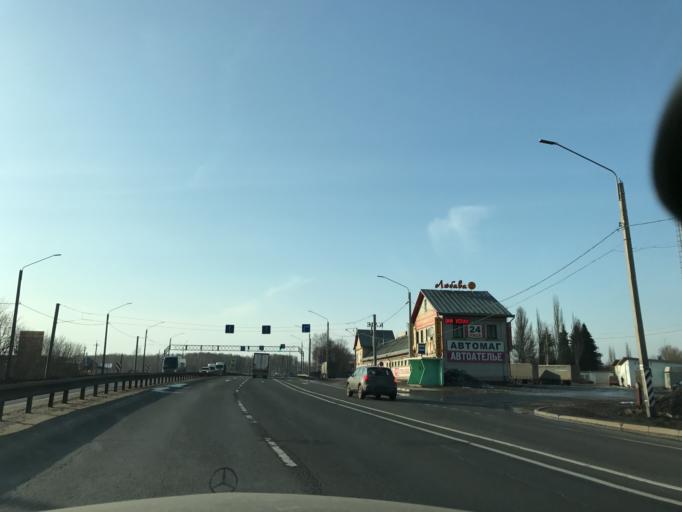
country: RU
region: Vladimir
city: Vyazniki
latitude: 56.2218
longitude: 42.1383
